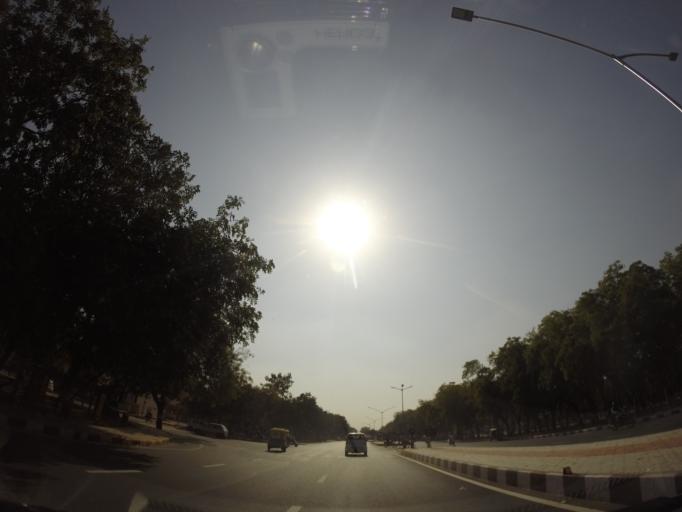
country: IN
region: Gujarat
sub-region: Gandhinagar
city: Ghandinagar
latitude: 23.2125
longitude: 72.6386
